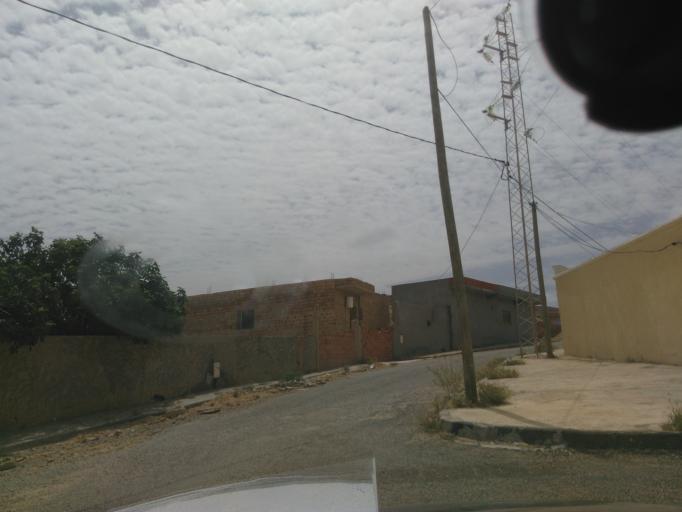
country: TN
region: Tataouine
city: Tataouine
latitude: 32.9451
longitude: 10.4658
